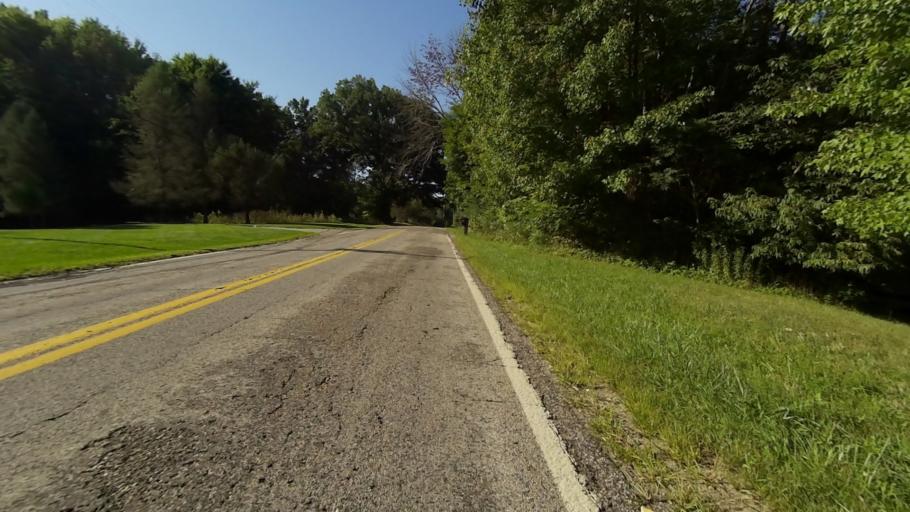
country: US
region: Ohio
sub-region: Portage County
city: Streetsboro
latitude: 41.2121
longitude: -81.3180
